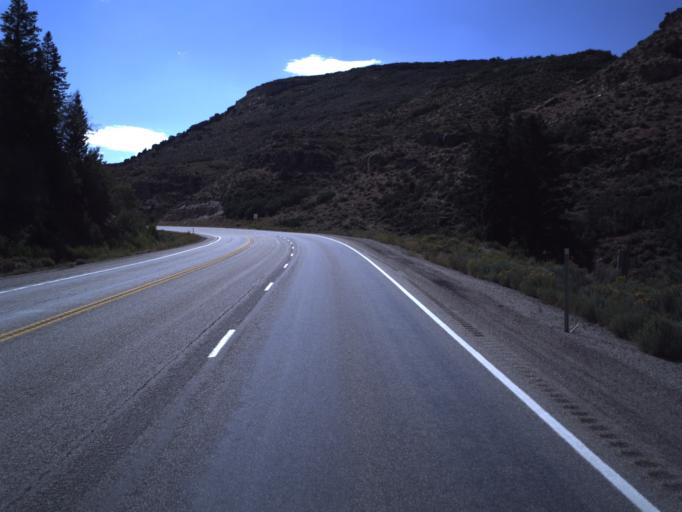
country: US
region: Utah
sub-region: Carbon County
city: Helper
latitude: 40.1946
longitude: -110.9430
